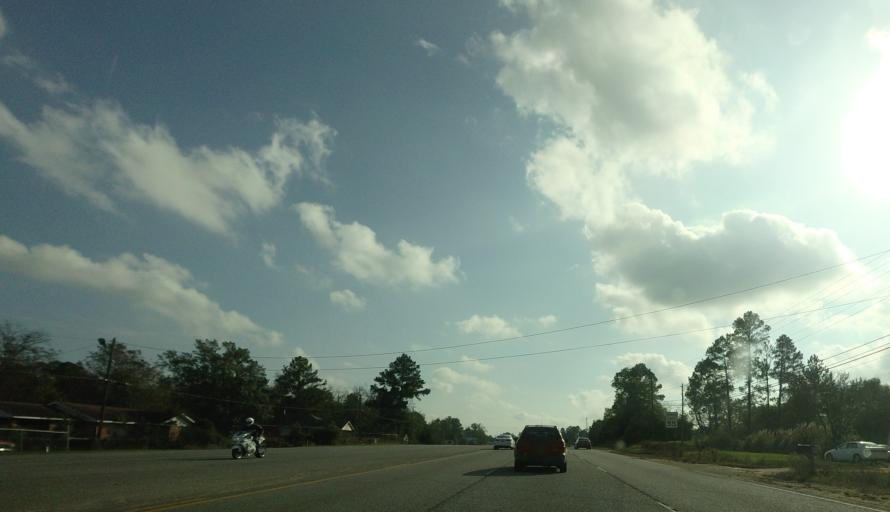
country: US
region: Georgia
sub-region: Bibb County
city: Macon
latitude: 32.7398
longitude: -83.6557
